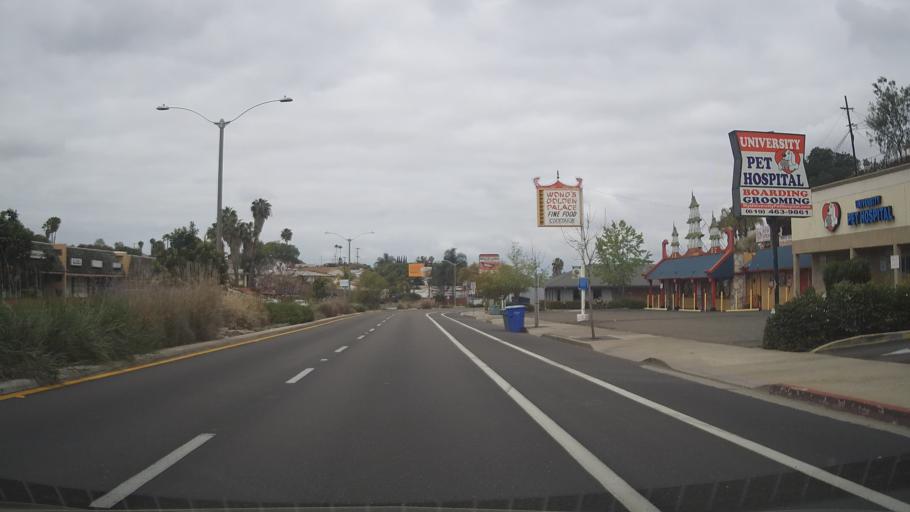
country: US
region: California
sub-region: San Diego County
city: Lemon Grove
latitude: 32.7551
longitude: -117.0444
